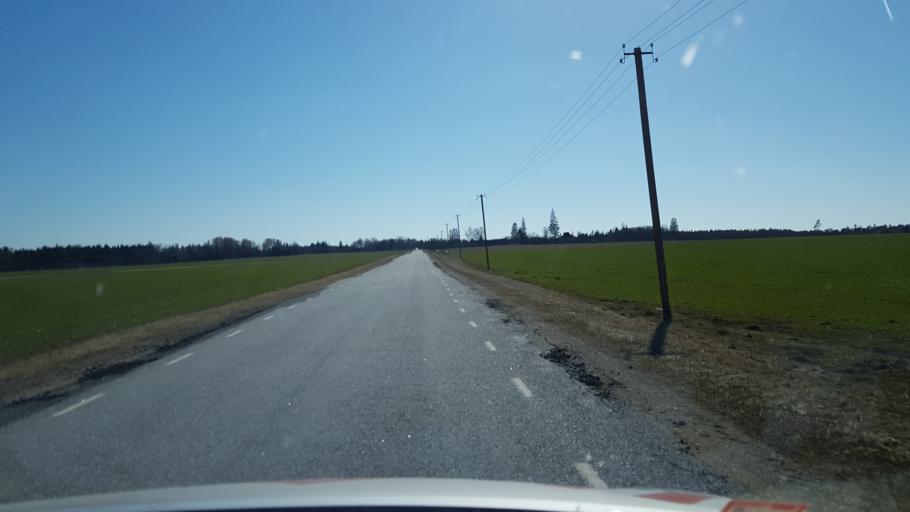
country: EE
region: Laeaene-Virumaa
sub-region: Tamsalu vald
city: Tamsalu
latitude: 59.0650
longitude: 26.1092
